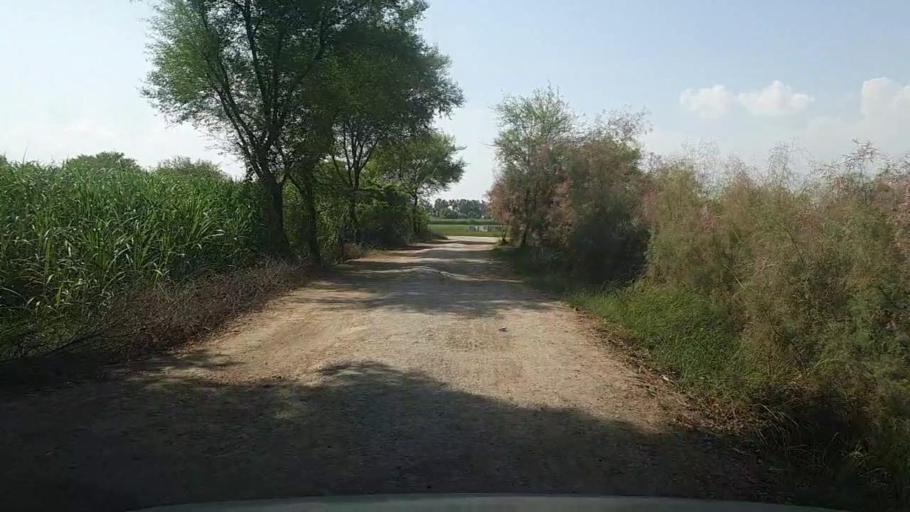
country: PK
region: Sindh
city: Khairpur
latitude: 28.1223
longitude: 69.6055
